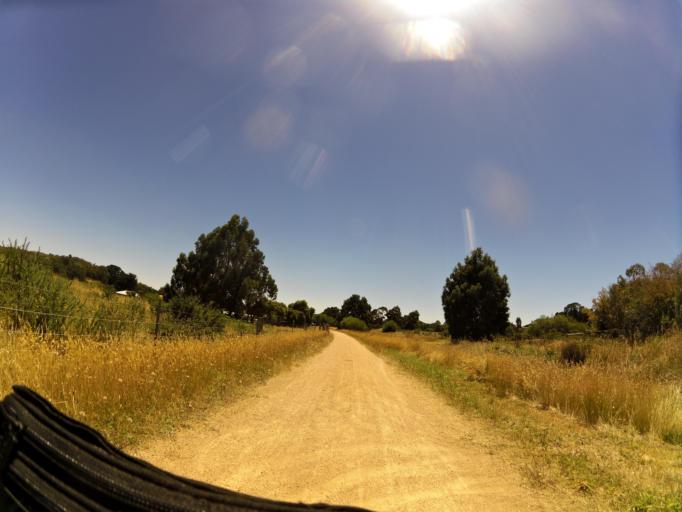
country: AU
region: Victoria
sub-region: Ballarat North
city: Delacombe
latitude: -37.6509
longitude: 143.6787
